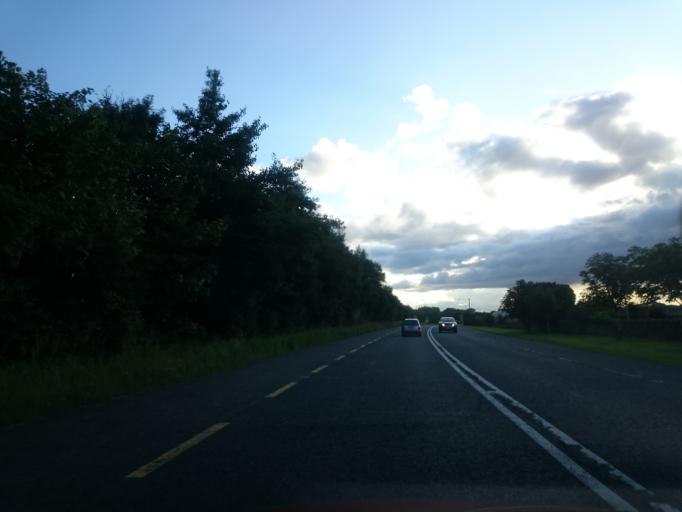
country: IE
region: Leinster
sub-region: Loch Garman
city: Rosslare
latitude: 52.2573
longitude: -6.4467
